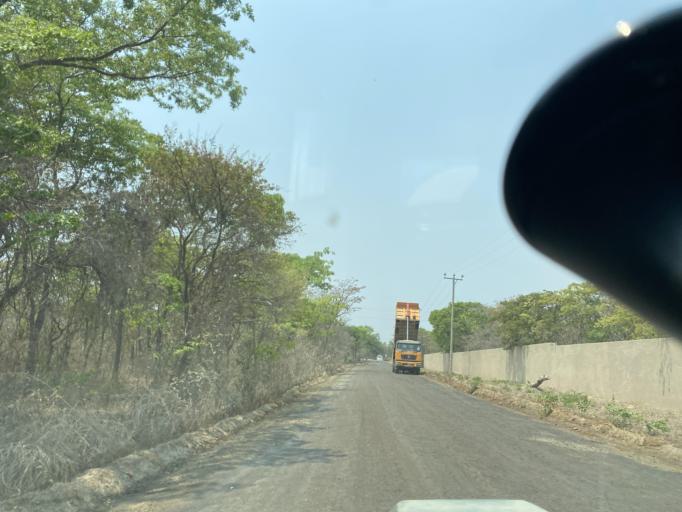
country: ZM
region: Lusaka
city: Lusaka
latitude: -15.5096
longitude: 28.4462
